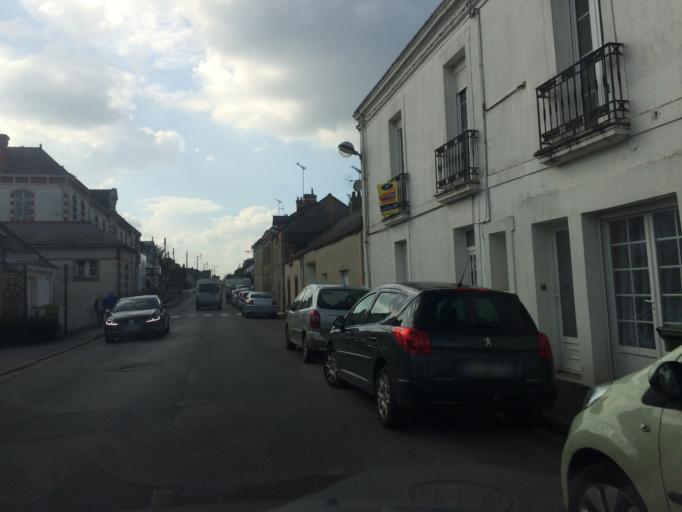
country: FR
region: Pays de la Loire
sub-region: Departement de la Loire-Atlantique
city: Blain
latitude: 47.4766
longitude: -1.7654
